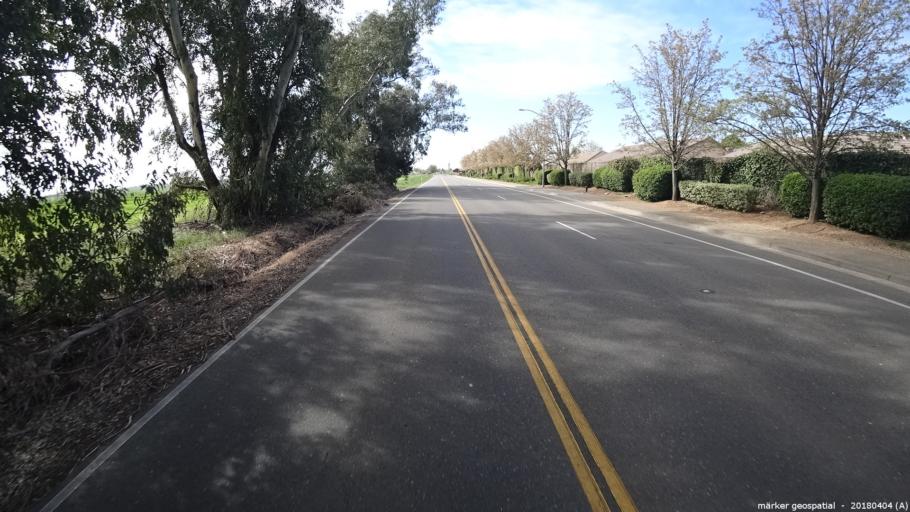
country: US
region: California
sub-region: Sacramento County
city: Galt
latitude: 38.2805
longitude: -121.2825
